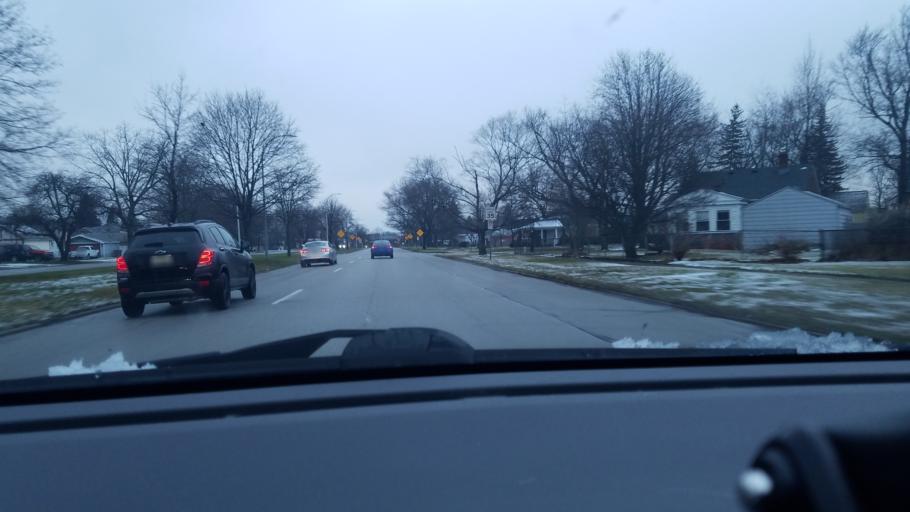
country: US
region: Michigan
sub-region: Wayne County
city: Dearborn Heights
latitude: 42.2966
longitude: -83.2592
